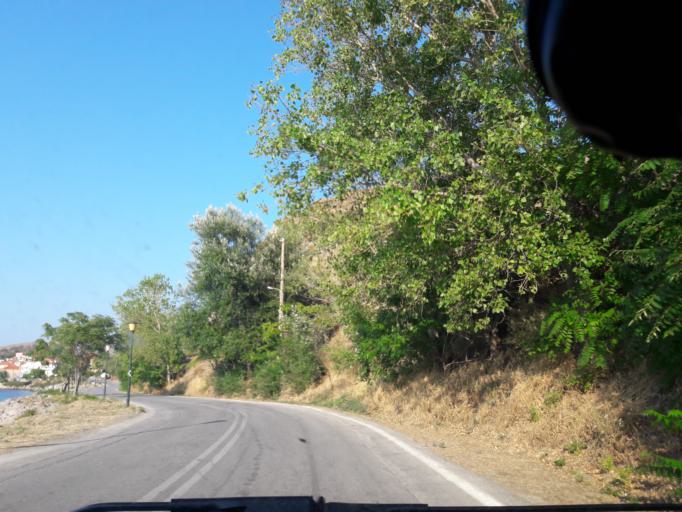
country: GR
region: North Aegean
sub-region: Nomos Lesvou
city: Myrina
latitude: 39.8694
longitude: 25.0582
